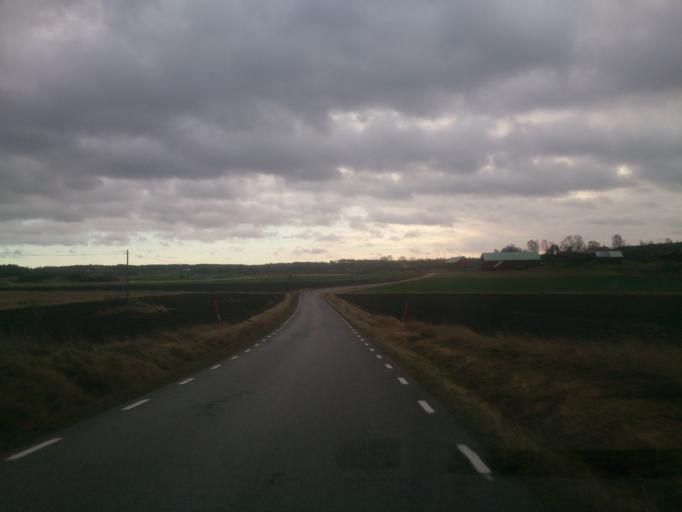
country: SE
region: OEstergoetland
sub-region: Norrkopings Kommun
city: Krokek
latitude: 58.5418
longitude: 16.6007
